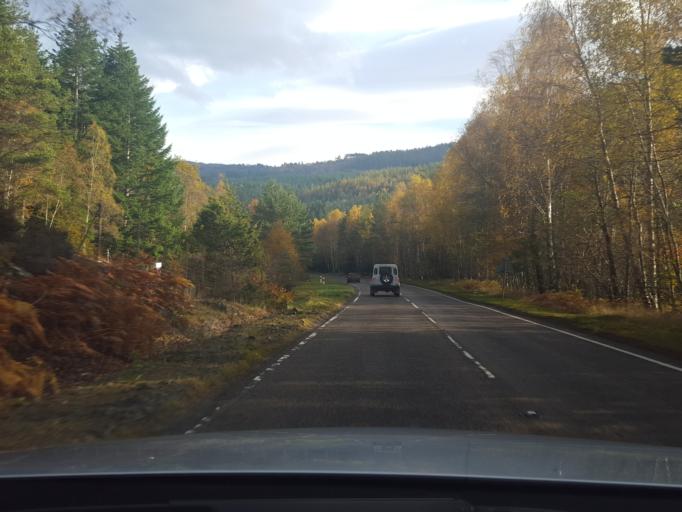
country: GB
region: Scotland
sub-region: Highland
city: Spean Bridge
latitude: 57.2019
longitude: -4.7099
